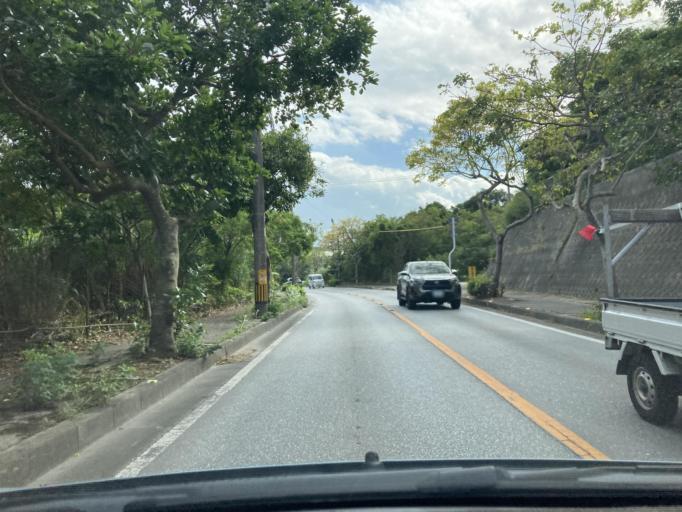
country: JP
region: Okinawa
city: Ginowan
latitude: 26.2749
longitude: 127.7810
